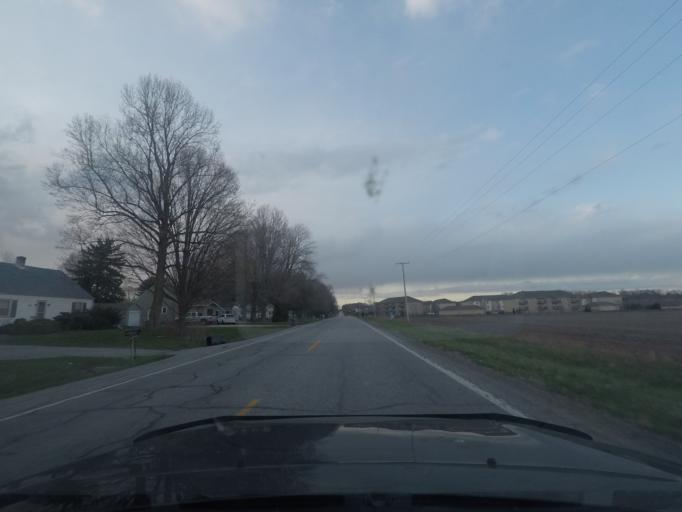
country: US
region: Indiana
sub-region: LaPorte County
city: LaPorte
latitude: 41.5862
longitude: -86.7391
